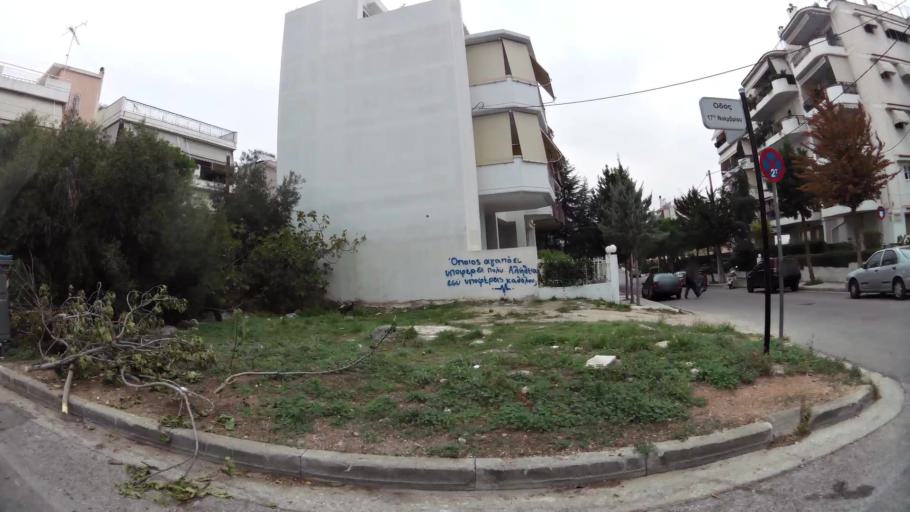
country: GR
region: Attica
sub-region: Nomarchia Athinas
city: Alimos
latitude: 37.9183
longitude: 23.7246
